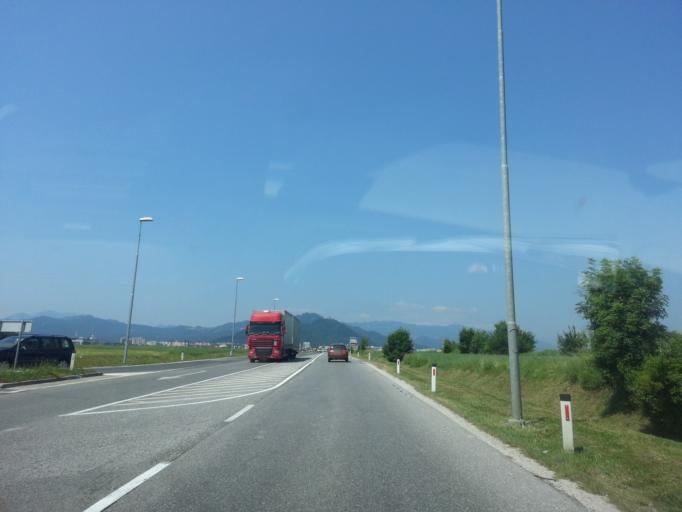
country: SI
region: Kranj
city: Britof
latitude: 46.2416
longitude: 14.3945
